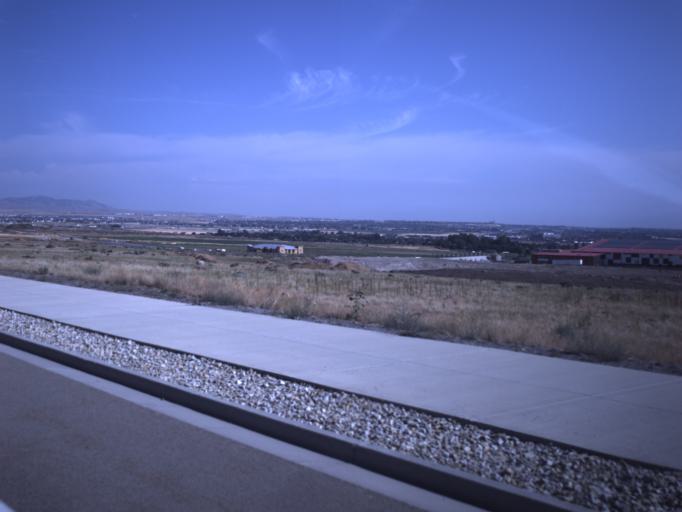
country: US
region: Utah
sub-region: Salt Lake County
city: Bluffdale
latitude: 40.4768
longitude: -111.9788
